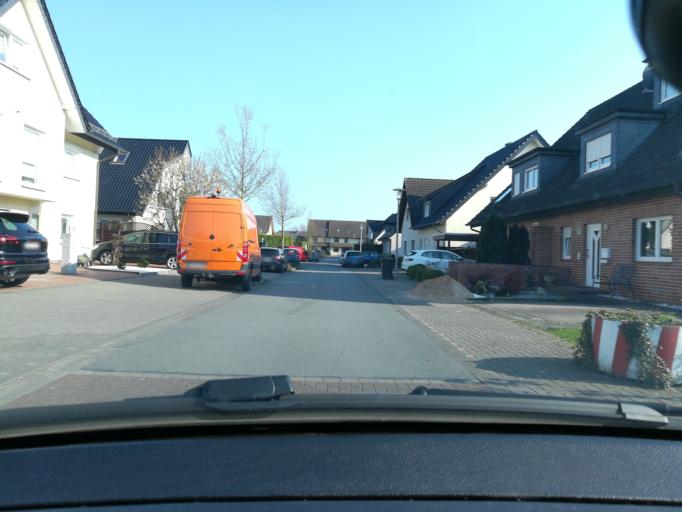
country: DE
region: North Rhine-Westphalia
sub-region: Regierungsbezirk Detmold
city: Oerlinghausen
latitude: 51.9307
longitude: 8.5997
